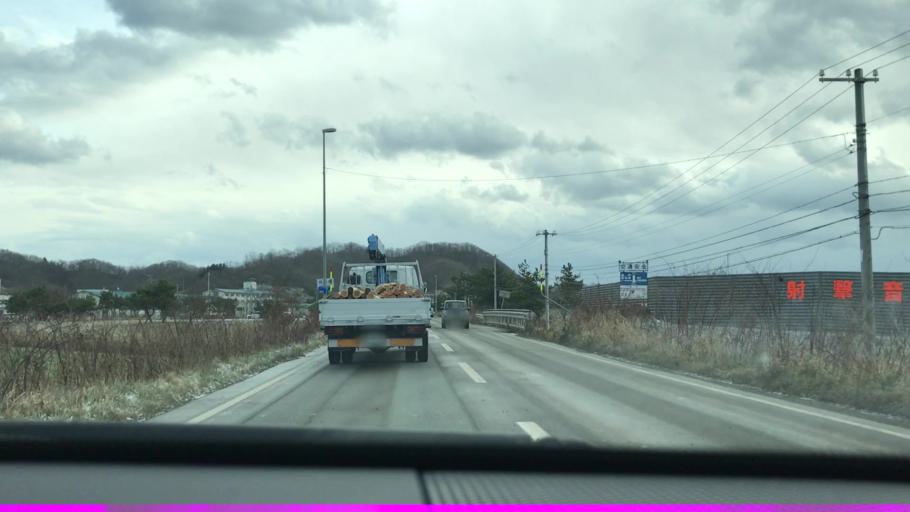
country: JP
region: Hokkaido
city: Shizunai-furukawacho
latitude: 42.3089
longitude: 142.4346
